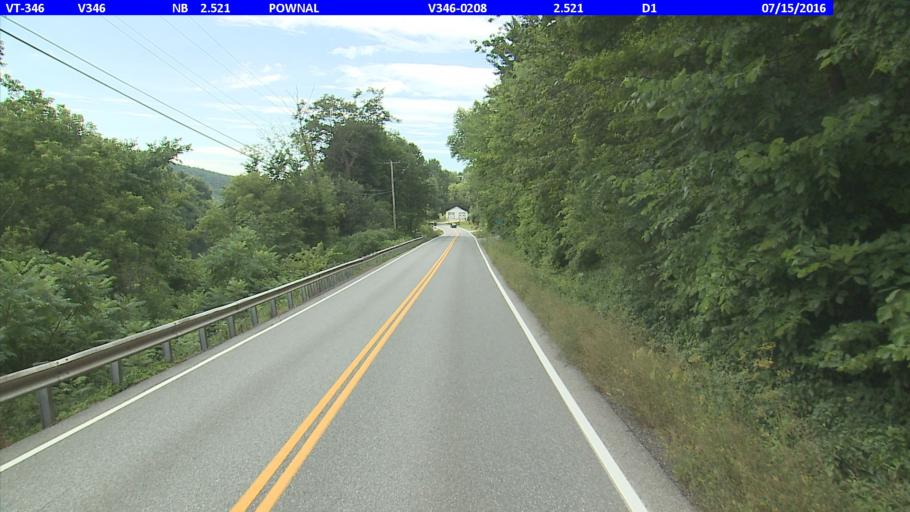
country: US
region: Massachusetts
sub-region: Berkshire County
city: Williamstown
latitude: 42.7932
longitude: -73.2575
